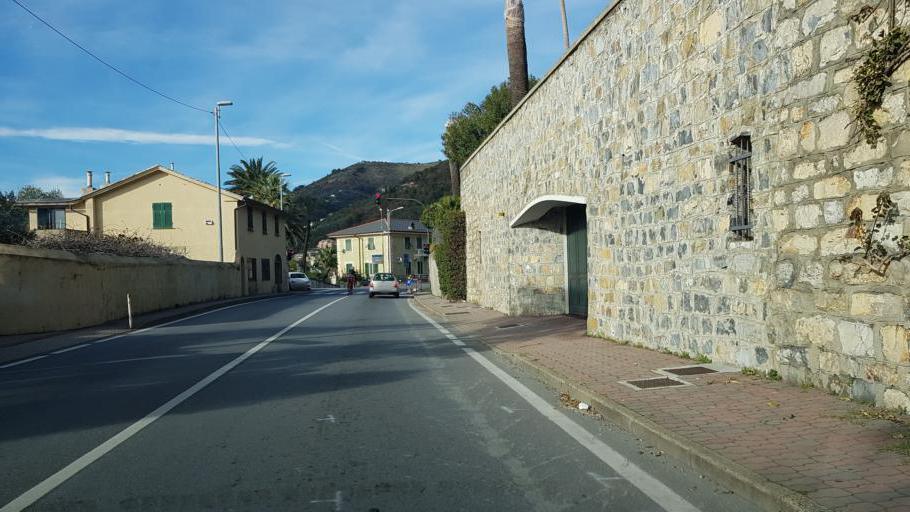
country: IT
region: Liguria
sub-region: Provincia di Genova
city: Pieve Ligure
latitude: 44.3737
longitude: 9.0860
